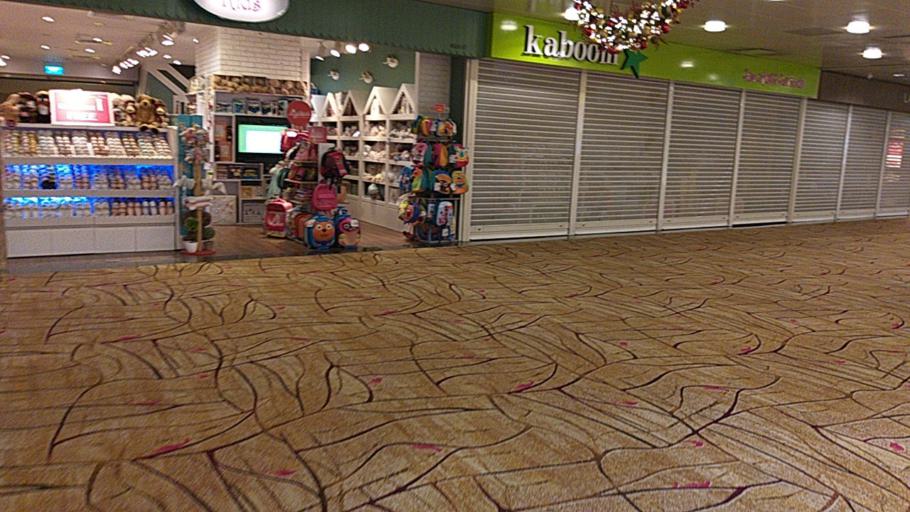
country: SG
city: Singapore
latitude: 1.3558
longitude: 103.9900
